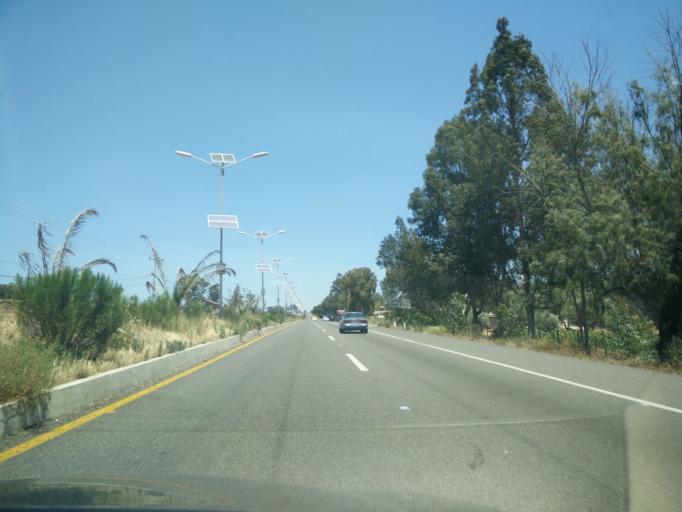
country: MX
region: Baja California
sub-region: Ensenada
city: Rancho Verde
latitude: 31.9825
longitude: -116.6481
